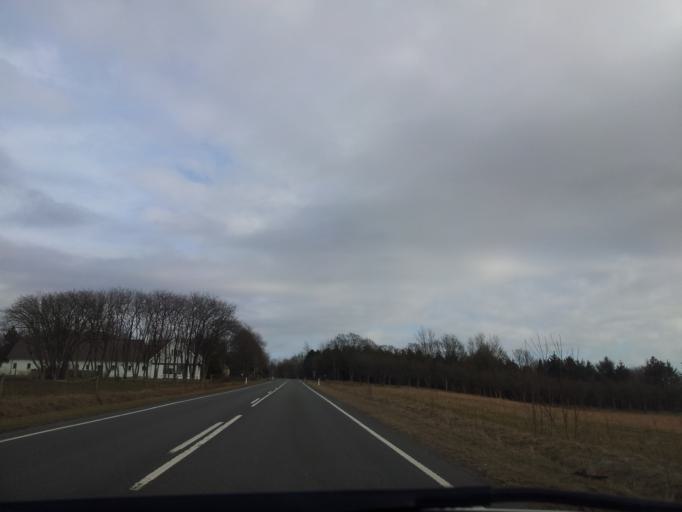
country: DK
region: South Denmark
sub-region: Vejen Kommune
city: Brorup
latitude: 55.4413
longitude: 9.0617
